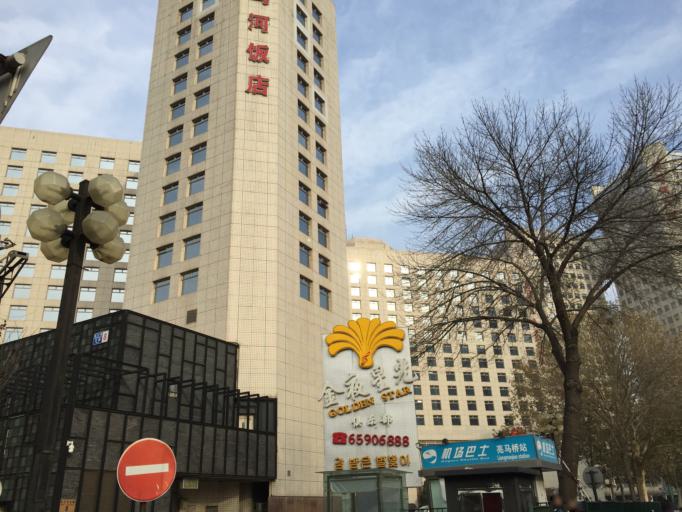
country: CN
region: Beijing
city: Chaowai
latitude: 39.9443
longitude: 116.4561
